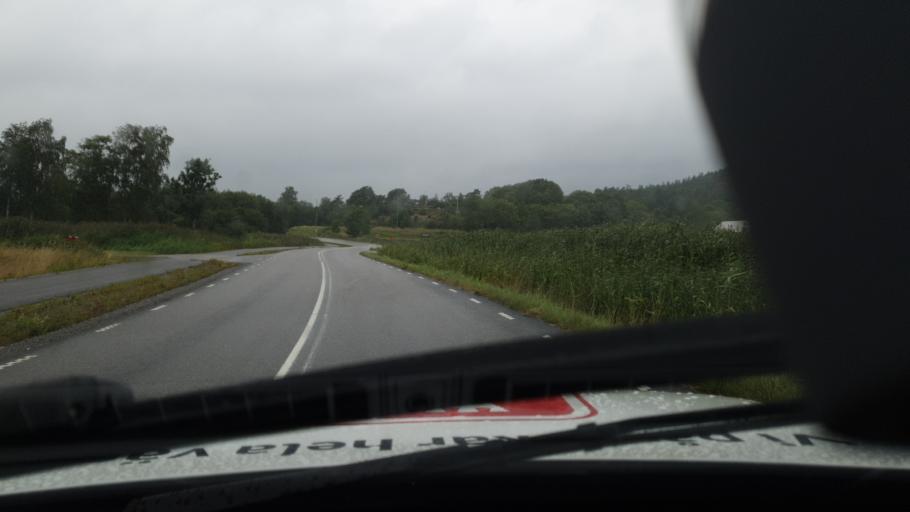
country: SE
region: Vaestra Goetaland
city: Svanesund
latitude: 58.1324
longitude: 11.8499
